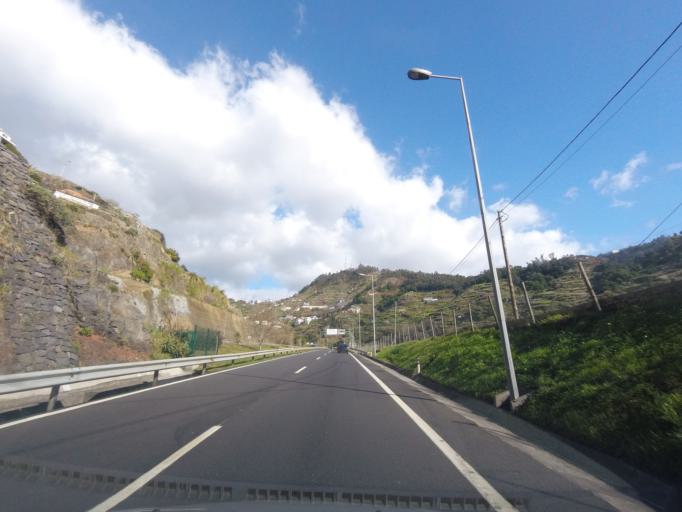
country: PT
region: Madeira
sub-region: Ribeira Brava
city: Campanario
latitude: 32.6583
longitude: -17.0203
